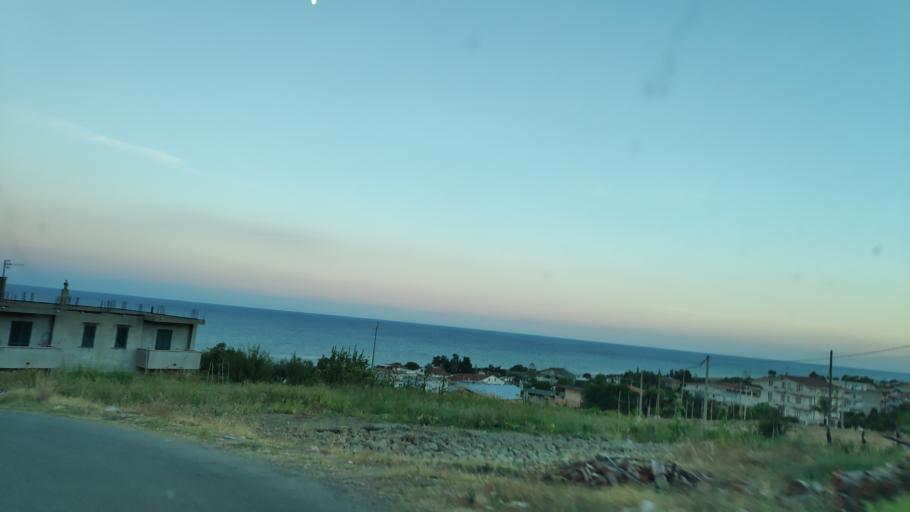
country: IT
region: Calabria
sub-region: Provincia di Reggio Calabria
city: Riace Marina
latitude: 38.3914
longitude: 16.5280
